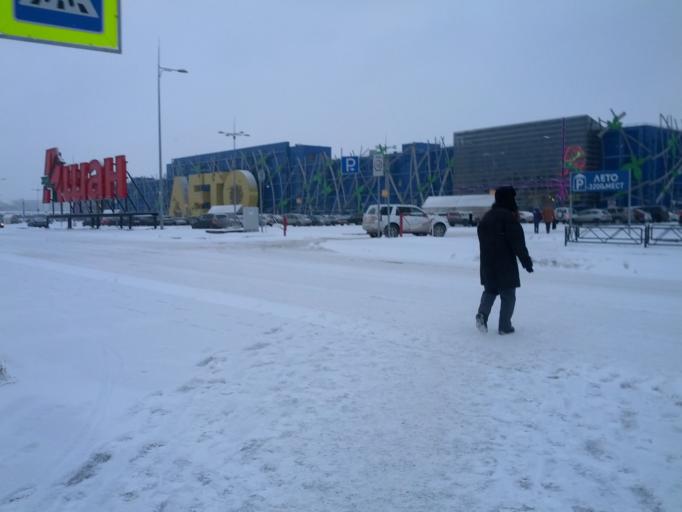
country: RU
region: St.-Petersburg
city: Kupchino
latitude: 59.8216
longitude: 30.3205
